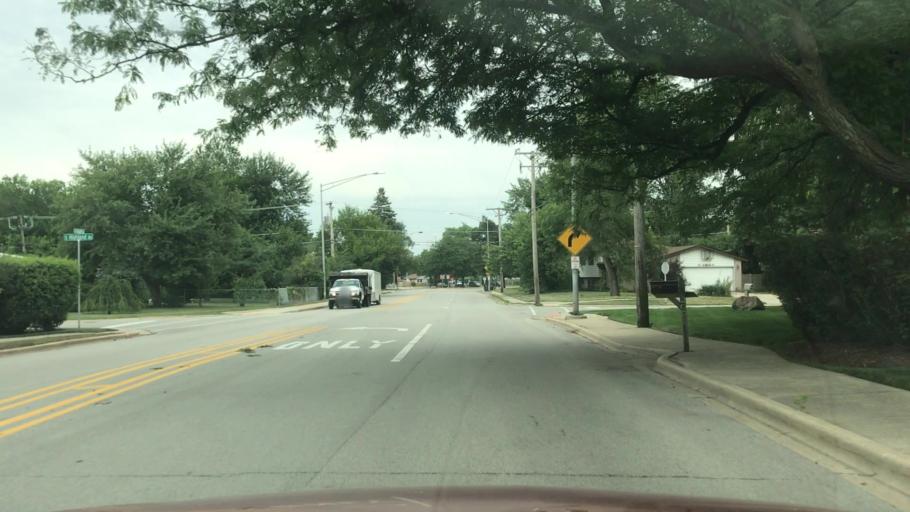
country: US
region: Illinois
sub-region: Cook County
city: Arlington Heights
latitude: 42.0677
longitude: -87.9860
